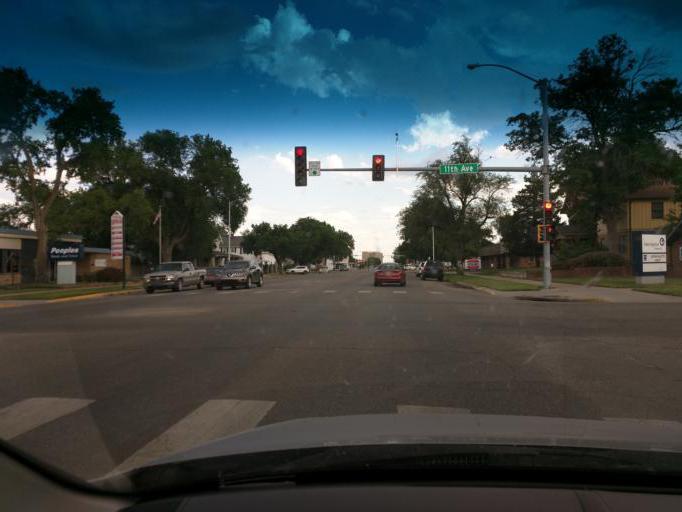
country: US
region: Kansas
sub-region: Reno County
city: Hutchinson
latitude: 38.0652
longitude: -97.9320
